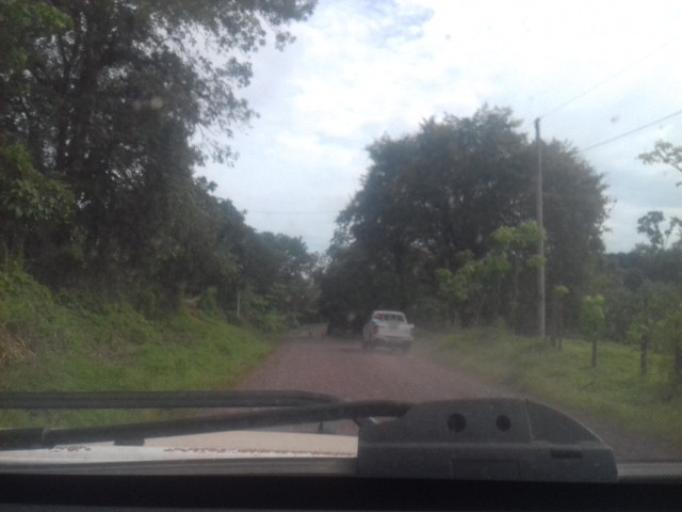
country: NI
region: Atlantico Norte (RAAN)
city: Waslala
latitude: 13.4352
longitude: -85.3096
